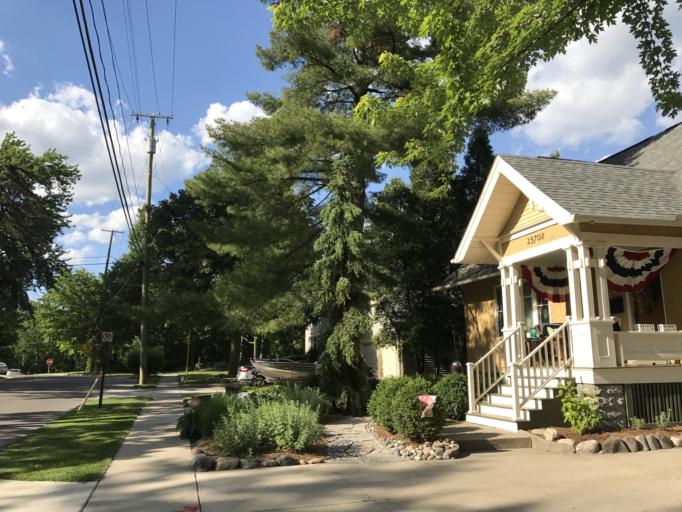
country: US
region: Michigan
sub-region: Oakland County
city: Farmington
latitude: 42.4656
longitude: -83.3734
